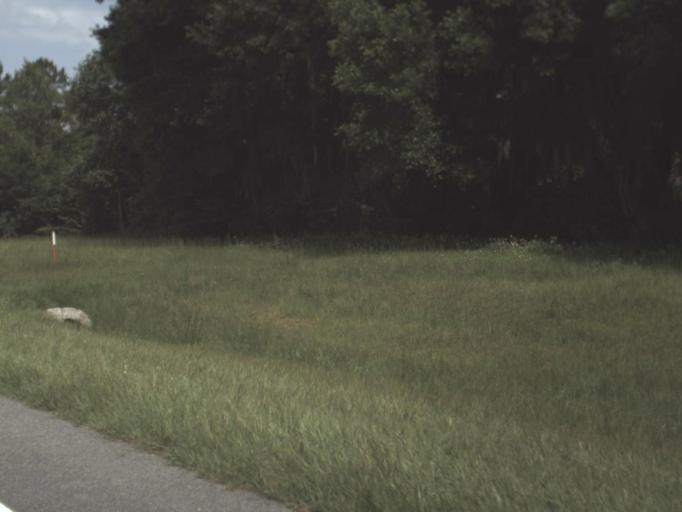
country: US
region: Florida
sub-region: Madison County
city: Madison
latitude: 30.4884
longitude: -83.4819
